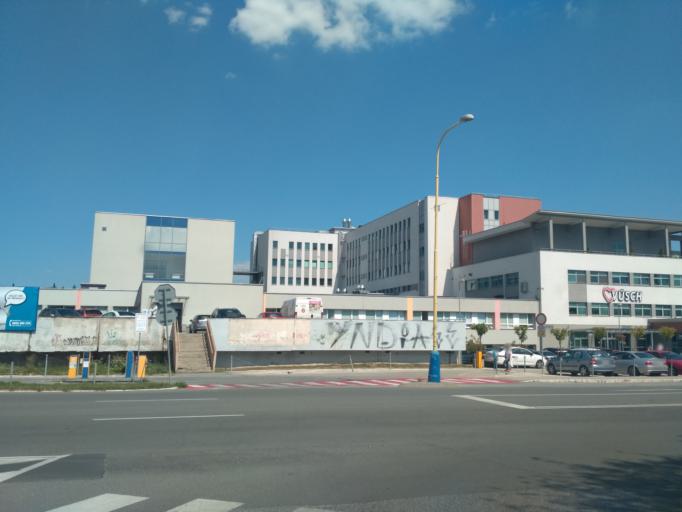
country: SK
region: Kosicky
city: Kosice
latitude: 48.7207
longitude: 21.2394
